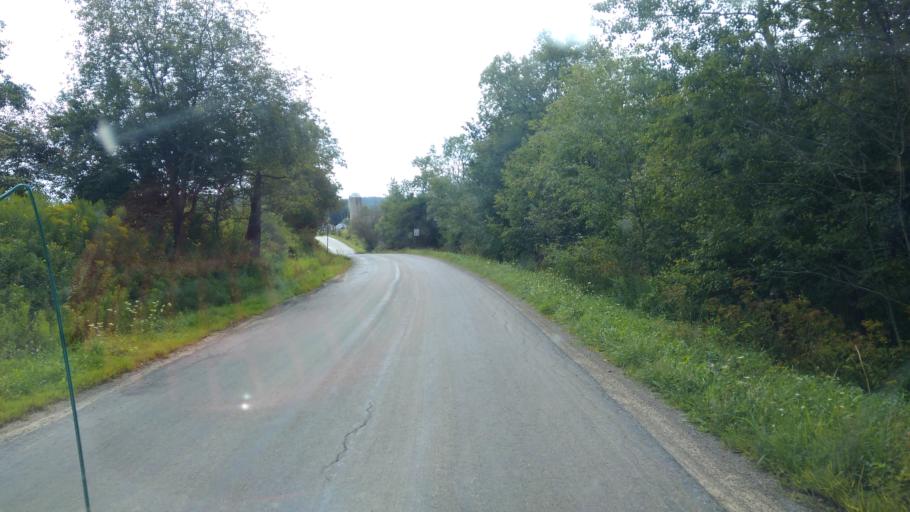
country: US
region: Pennsylvania
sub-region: Tioga County
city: Westfield
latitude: 41.9229
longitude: -77.7570
